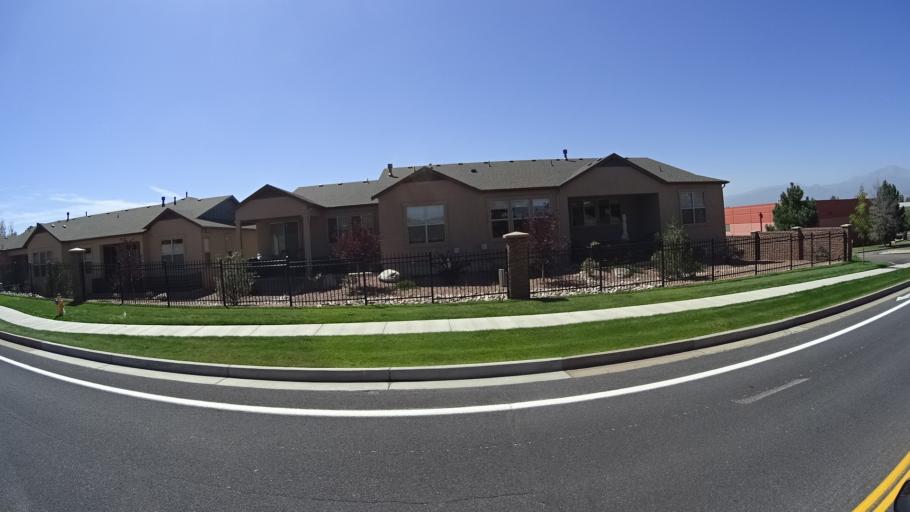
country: US
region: Colorado
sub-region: El Paso County
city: Black Forest
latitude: 38.9475
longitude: -104.7642
